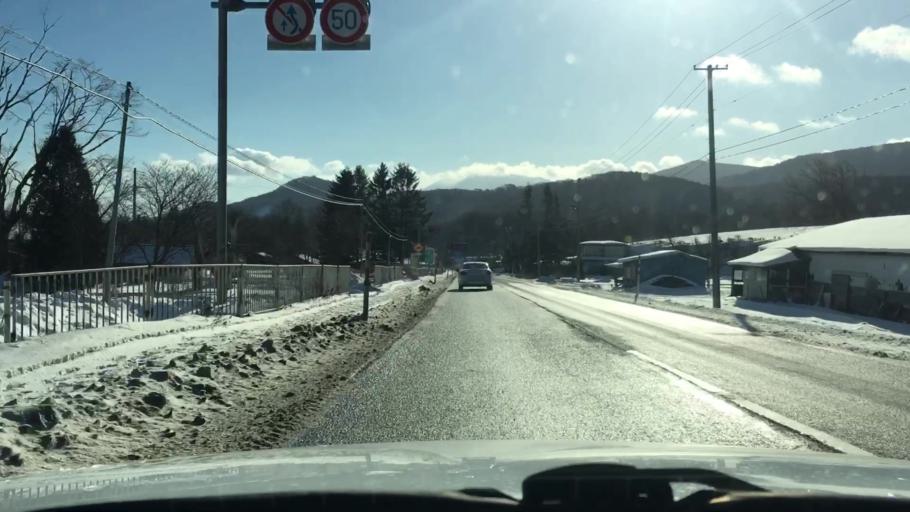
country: JP
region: Iwate
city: Morioka-shi
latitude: 39.6500
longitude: 141.3550
